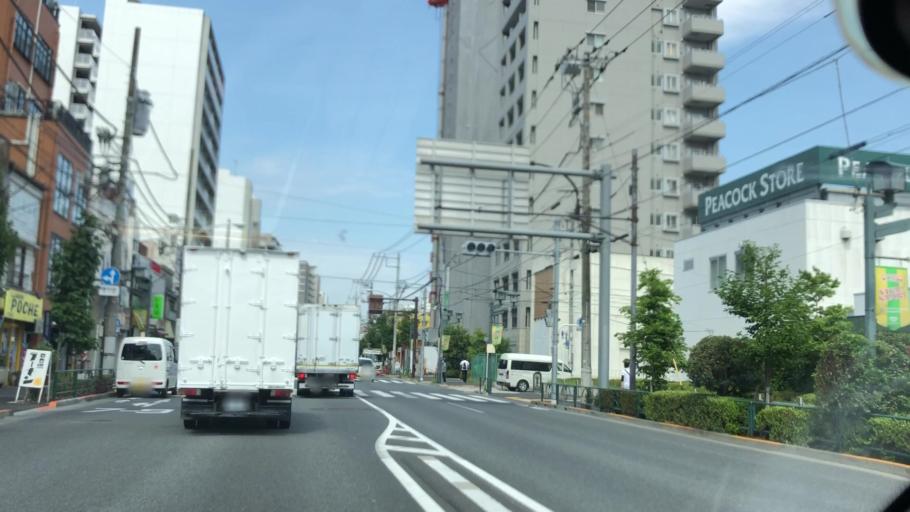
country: JP
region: Tokyo
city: Urayasu
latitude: 35.6895
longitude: 139.8327
